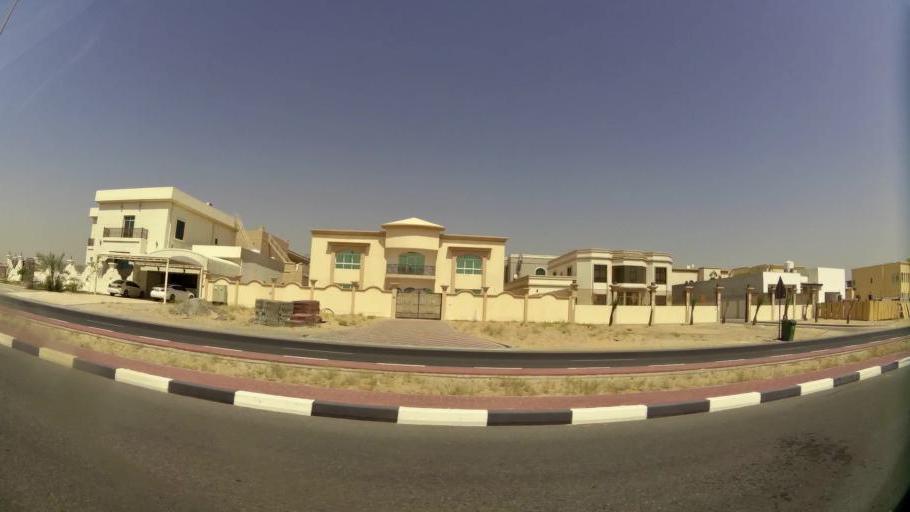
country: AE
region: Ajman
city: Ajman
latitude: 25.4149
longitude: 55.5283
